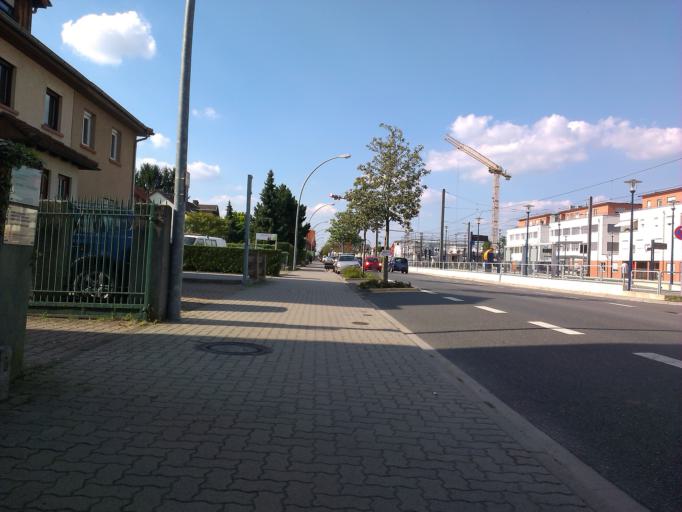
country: DE
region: Baden-Wuerttemberg
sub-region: Karlsruhe Region
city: Schriesheim
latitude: 49.4714
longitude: 8.6601
